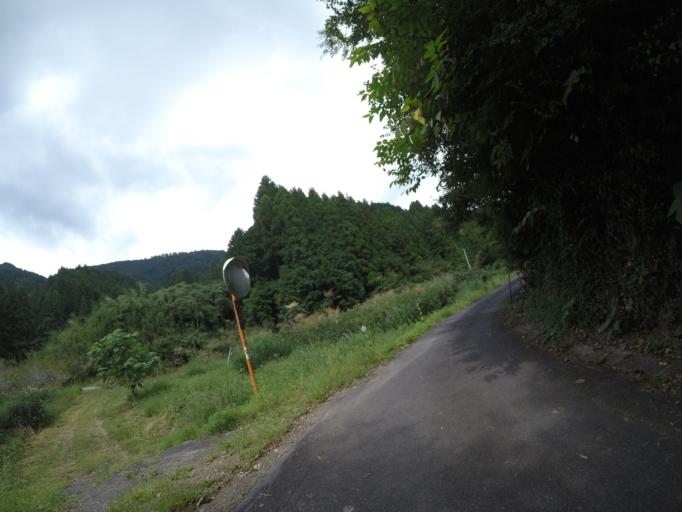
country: JP
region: Shizuoka
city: Shimada
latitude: 34.8870
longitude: 138.1673
